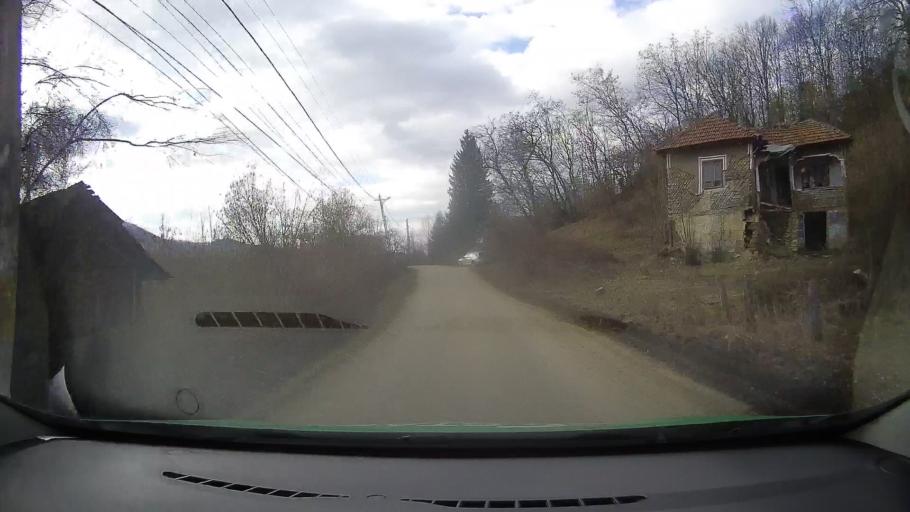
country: RO
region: Prahova
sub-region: Comuna Adunati
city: Adunati
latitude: 45.1157
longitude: 25.5878
